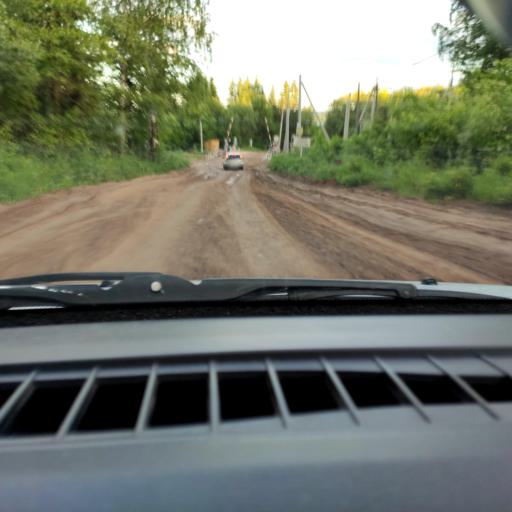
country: RU
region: Perm
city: Polazna
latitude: 58.1979
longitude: 56.4757
